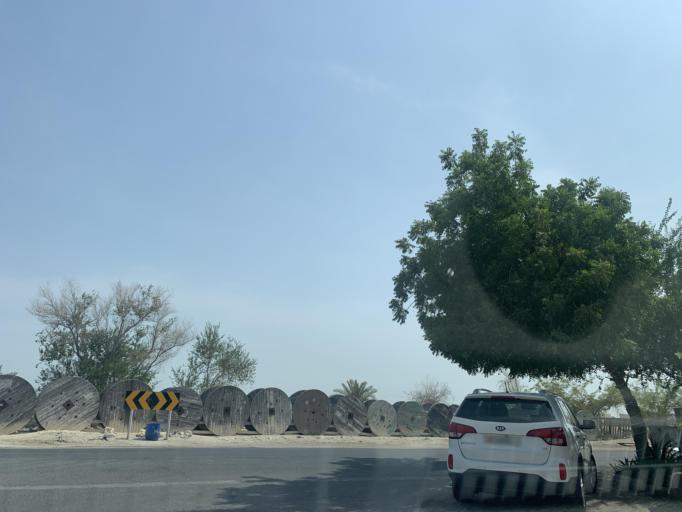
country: BH
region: Muharraq
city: Al Hadd
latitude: 26.2635
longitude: 50.6571
